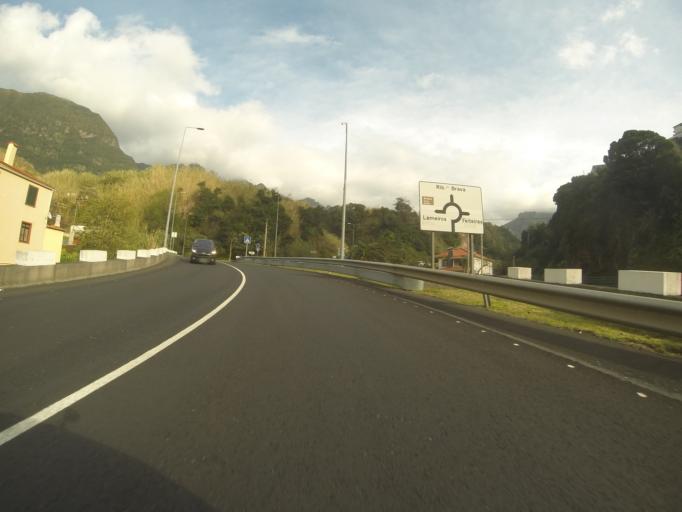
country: PT
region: Madeira
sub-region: Sao Vicente
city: Sao Vicente
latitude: 32.7923
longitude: -17.0350
